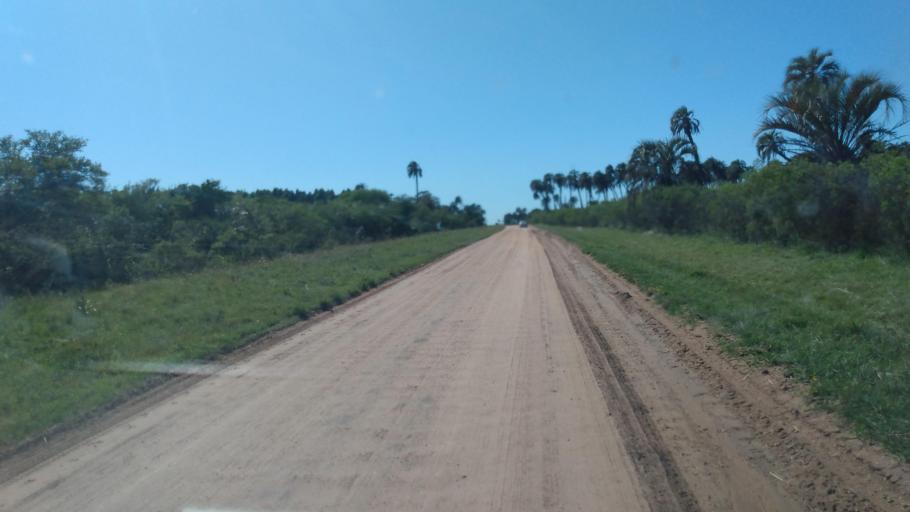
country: AR
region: Entre Rios
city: Ubajay
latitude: -31.8514
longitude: -58.2999
